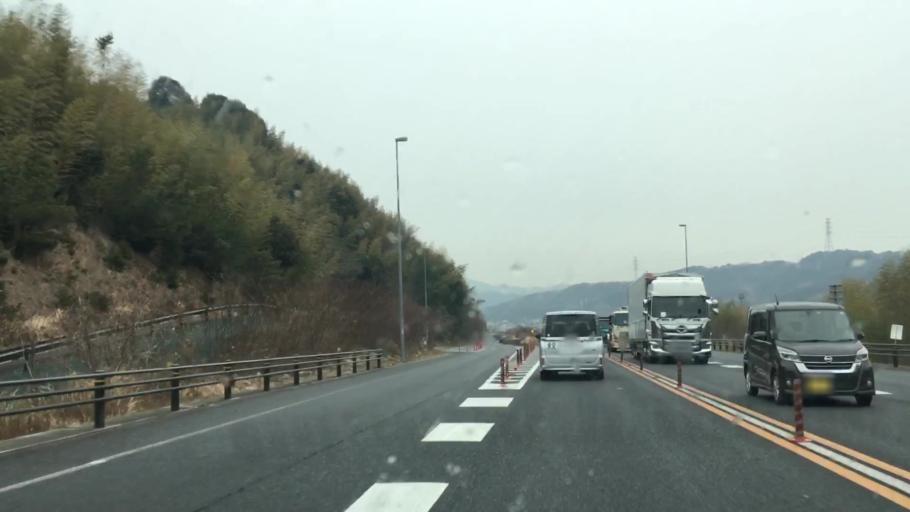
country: JP
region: Aichi
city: Gamagori
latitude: 34.8475
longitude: 137.1446
